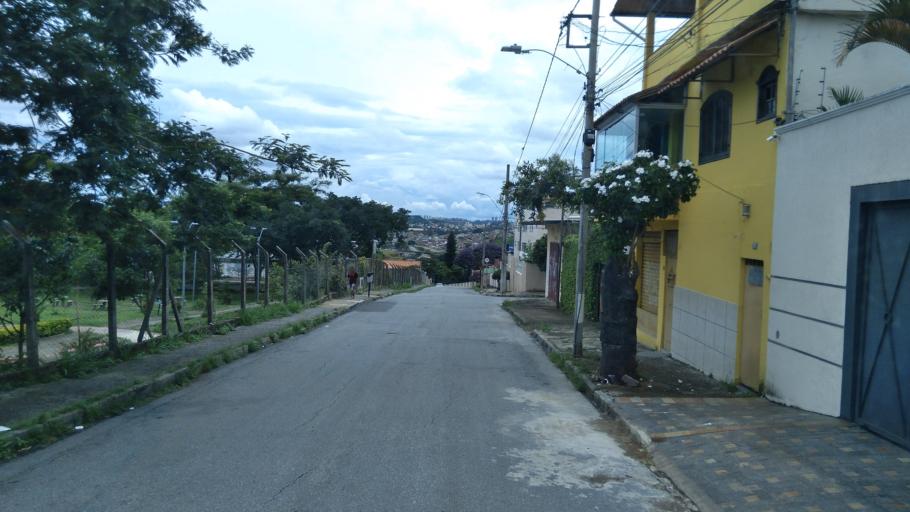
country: BR
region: Minas Gerais
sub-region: Belo Horizonte
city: Belo Horizonte
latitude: -19.8567
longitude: -43.9157
